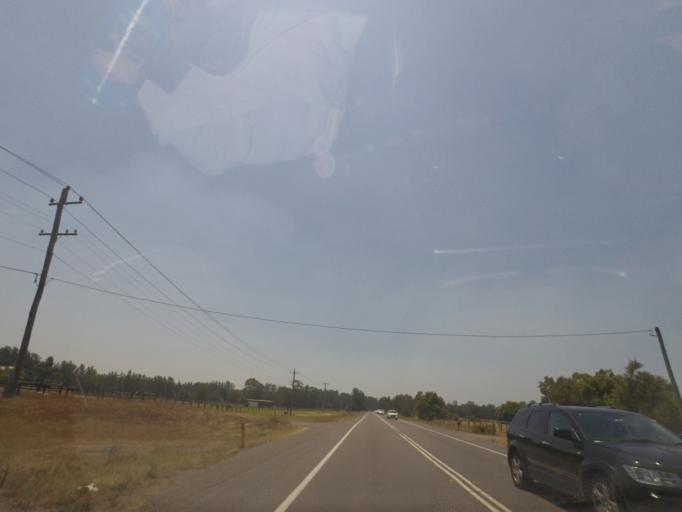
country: AU
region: New South Wales
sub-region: Port Stephens Shire
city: Medowie
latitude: -32.8059
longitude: 151.8768
